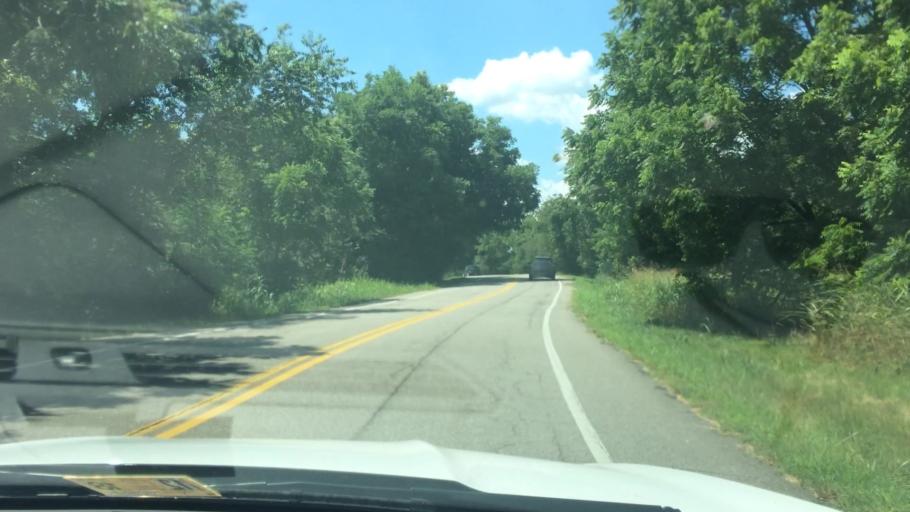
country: US
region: Virginia
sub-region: King William County
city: West Point
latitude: 37.5424
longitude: -76.7942
